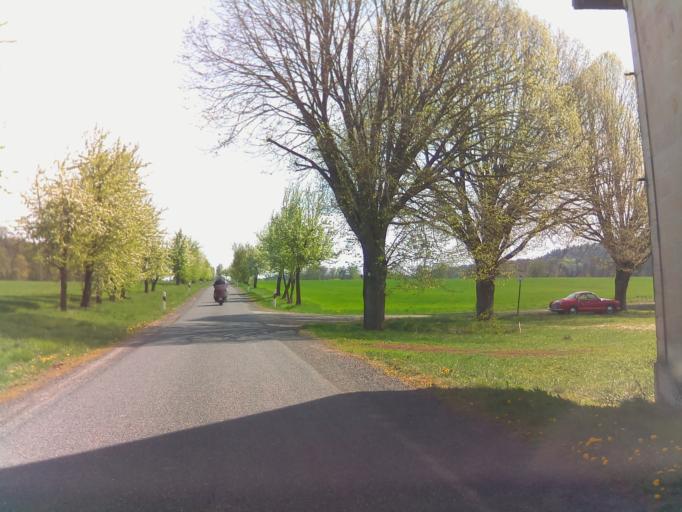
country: DE
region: Bavaria
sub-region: Regierungsbezirk Unterfranken
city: Ermershausen
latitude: 50.1861
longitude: 10.6210
